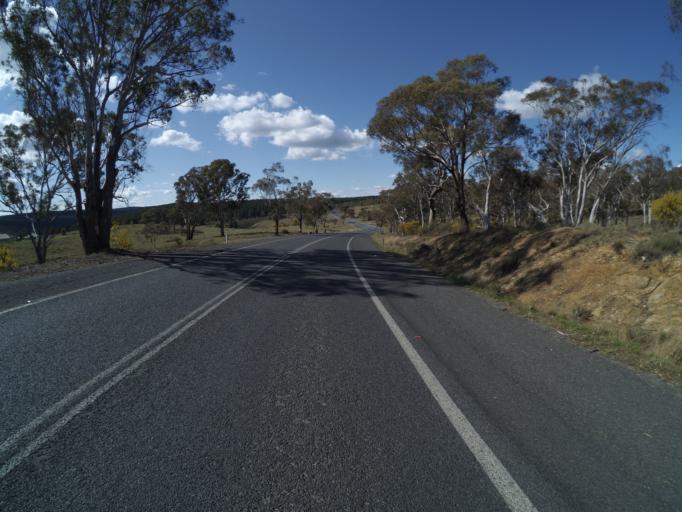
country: AU
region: New South Wales
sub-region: Queanbeyan
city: Queanbeyan
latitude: -35.3411
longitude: 149.2839
